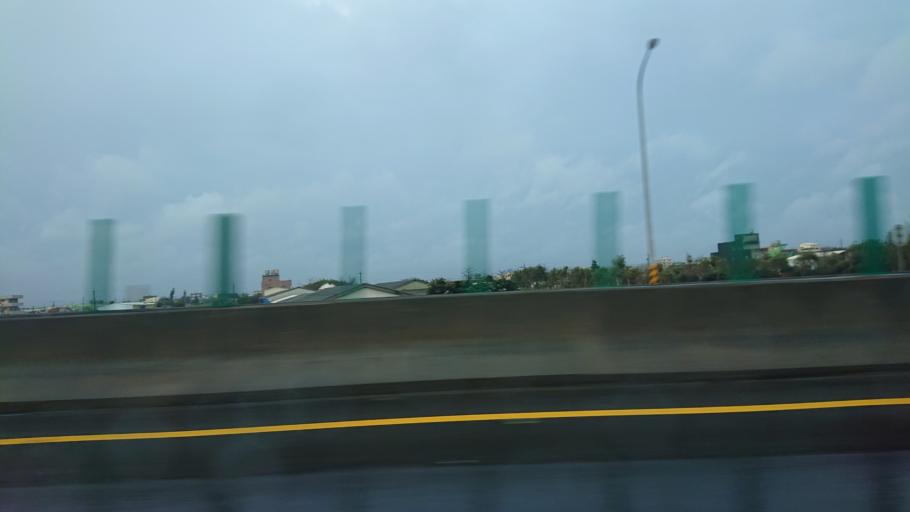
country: TW
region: Taiwan
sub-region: Changhua
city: Chang-hua
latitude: 24.1384
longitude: 120.4436
